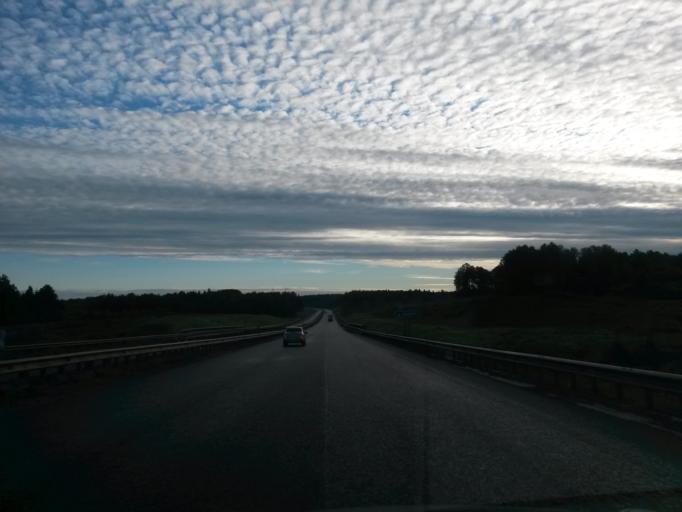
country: RU
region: Vladimir
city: Strunino
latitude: 56.5347
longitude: 38.5806
